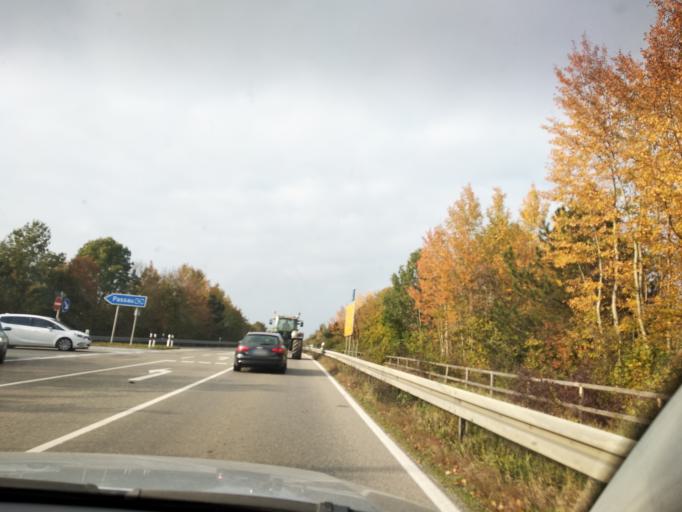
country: DE
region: Bavaria
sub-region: Upper Bavaria
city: Forstinning
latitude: 48.1689
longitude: 11.8917
